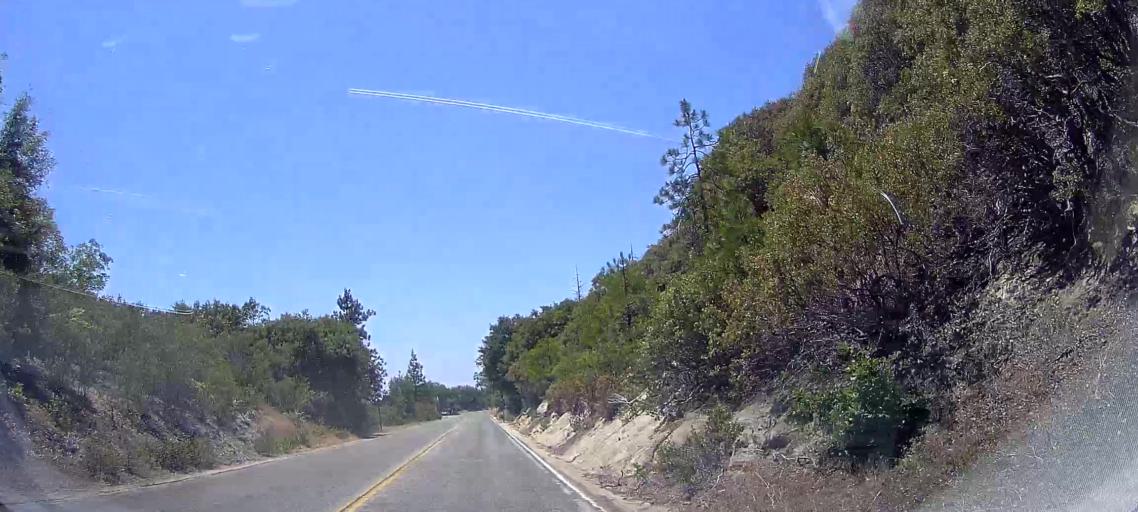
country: US
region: California
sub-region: Fresno County
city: Squaw Valley
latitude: 36.7416
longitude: -119.0295
